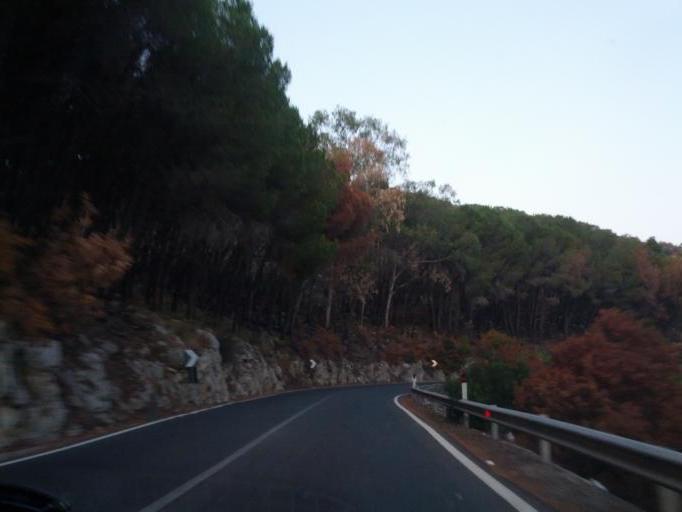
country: IT
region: Latium
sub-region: Provincia di Latina
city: Itri
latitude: 41.3134
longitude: 13.4915
